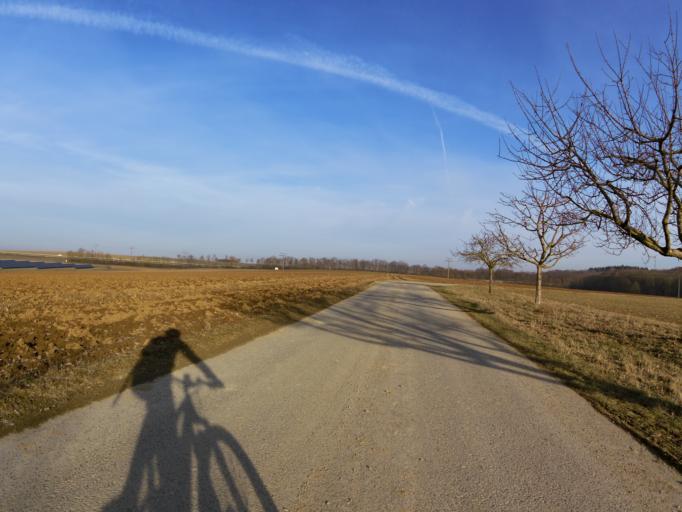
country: DE
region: Bavaria
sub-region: Regierungsbezirk Unterfranken
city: Kurnach
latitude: 49.8319
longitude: 10.0313
